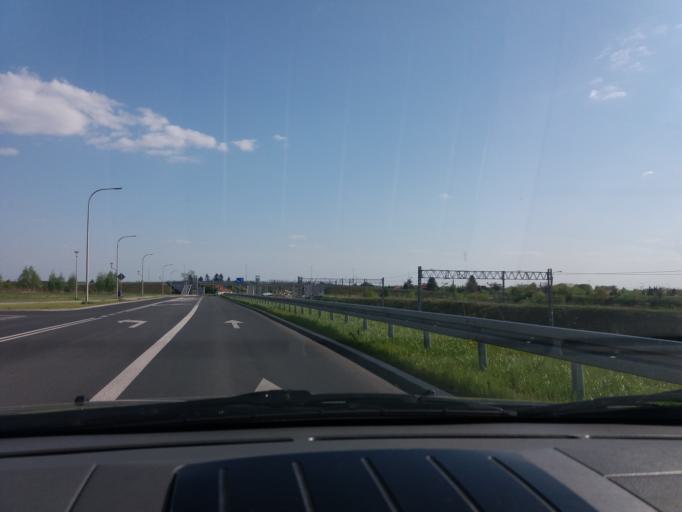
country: PL
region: Masovian Voivodeship
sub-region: Powiat mlawski
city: Mlawa
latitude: 53.1113
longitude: 20.3628
